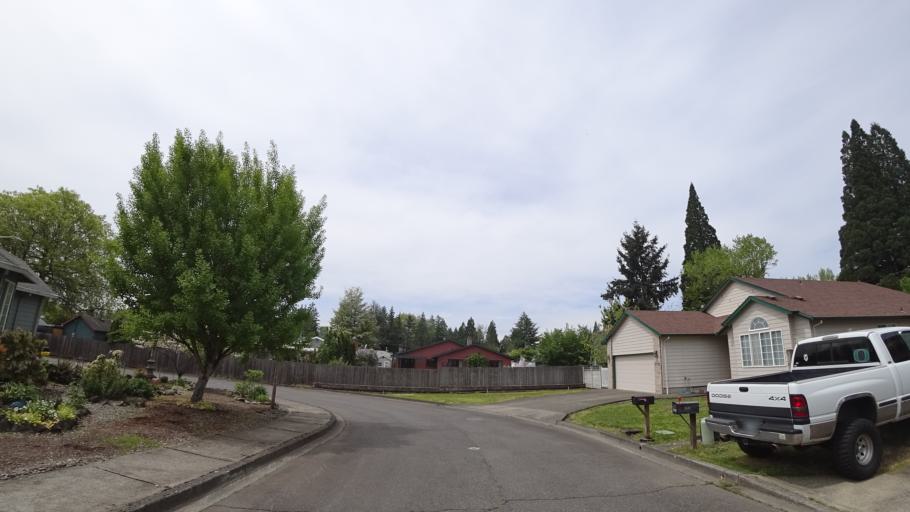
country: US
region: Oregon
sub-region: Clackamas County
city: Milwaukie
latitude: 45.4543
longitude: -122.6177
